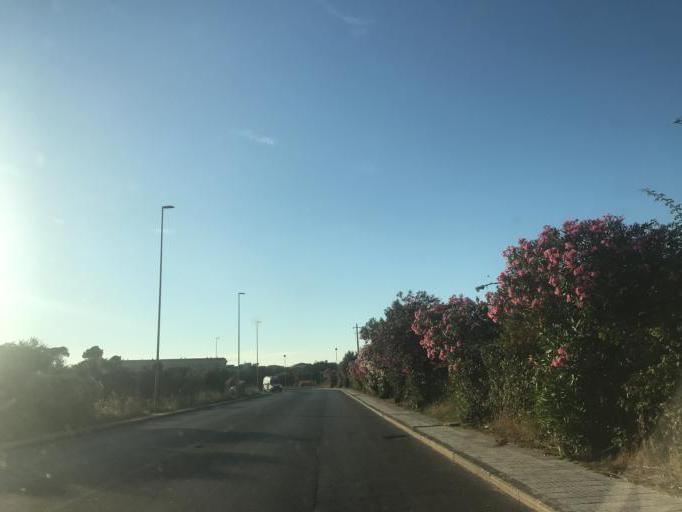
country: IT
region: Sardinia
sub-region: Provincia di Sassari
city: Alghero
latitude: 40.5686
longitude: 8.3290
